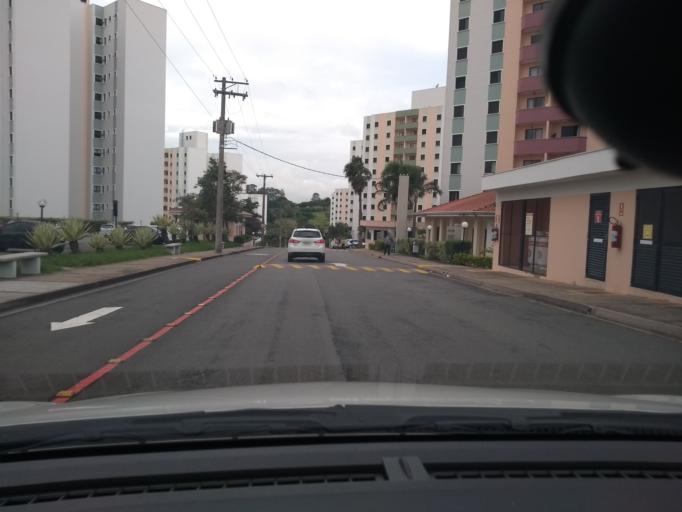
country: BR
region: Sao Paulo
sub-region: Jundiai
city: Jundiai
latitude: -23.1898
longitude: -46.9592
